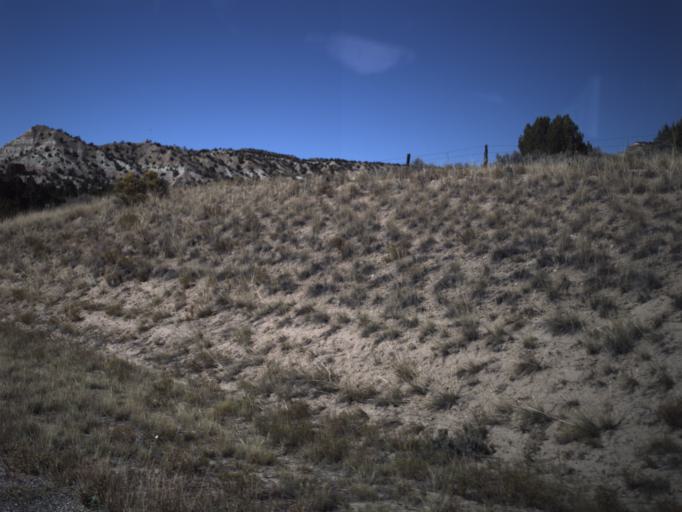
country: US
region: Utah
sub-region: Garfield County
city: Panguitch
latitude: 37.5624
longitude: -112.0317
